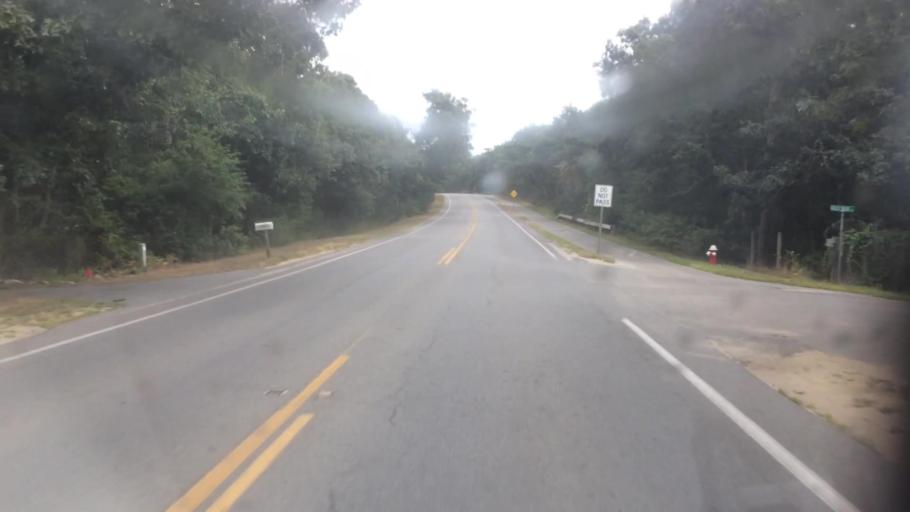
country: US
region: Massachusetts
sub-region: Dukes County
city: Edgartown
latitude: 41.3993
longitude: -70.5461
